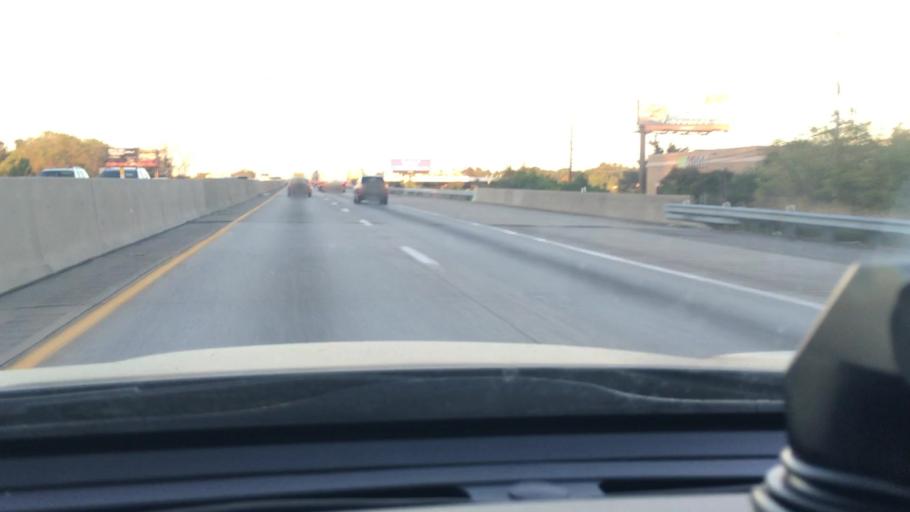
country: US
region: Pennsylvania
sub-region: Lehigh County
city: Fullerton
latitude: 40.6383
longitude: -75.4468
